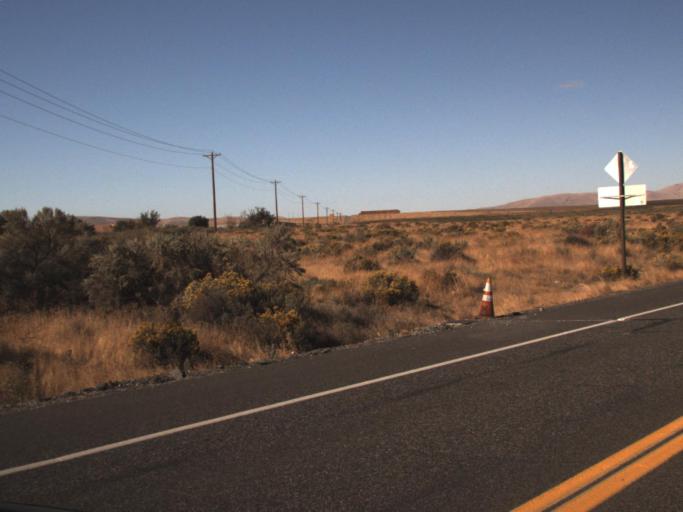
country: US
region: Washington
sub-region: Benton County
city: Richland
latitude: 46.3151
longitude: -119.2957
